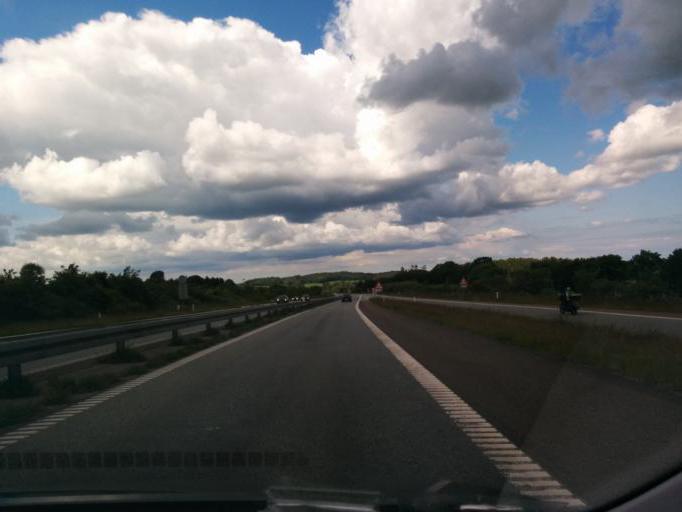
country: DK
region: Central Jutland
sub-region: Syddjurs Kommune
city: Ronde
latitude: 56.3044
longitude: 10.5055
